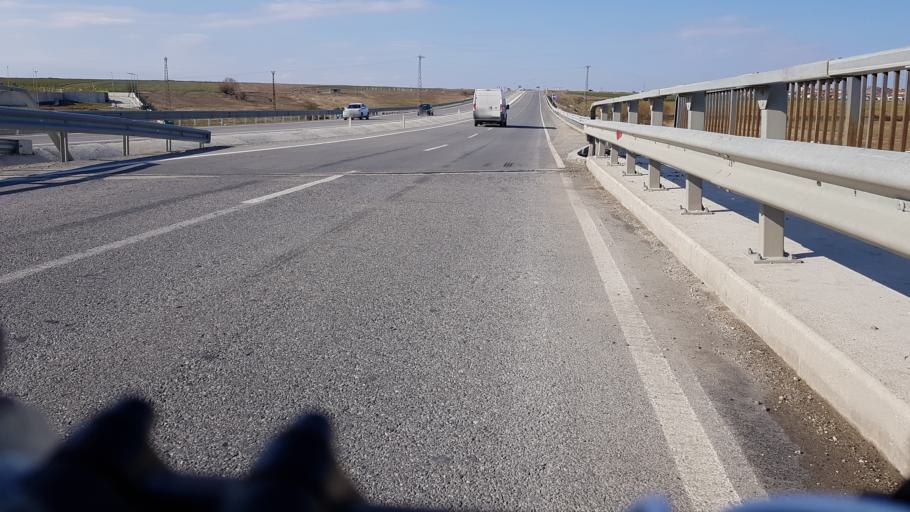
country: TR
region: Tekirdag
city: Saray
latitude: 41.4254
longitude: 27.9126
